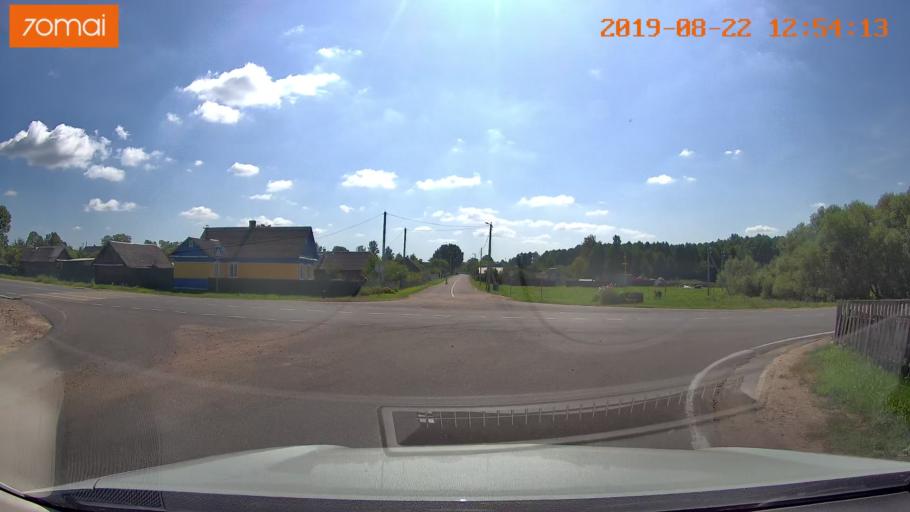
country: BY
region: Minsk
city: Prawdzinski
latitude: 53.4380
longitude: 27.6930
